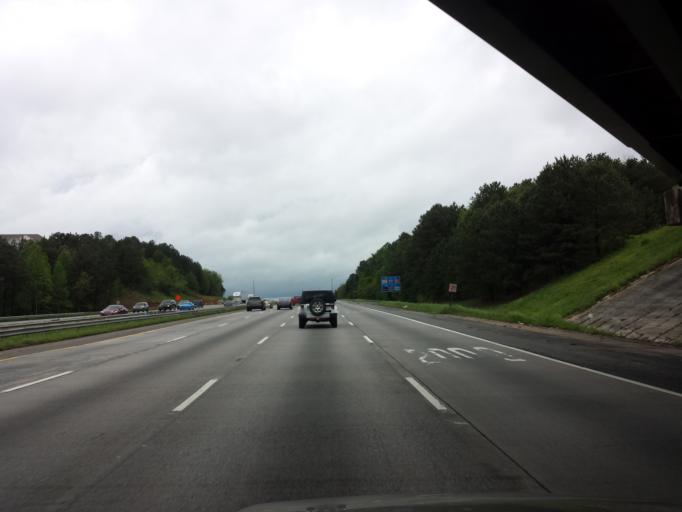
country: US
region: Georgia
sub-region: Cobb County
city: Marietta
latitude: 34.0005
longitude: -84.5621
